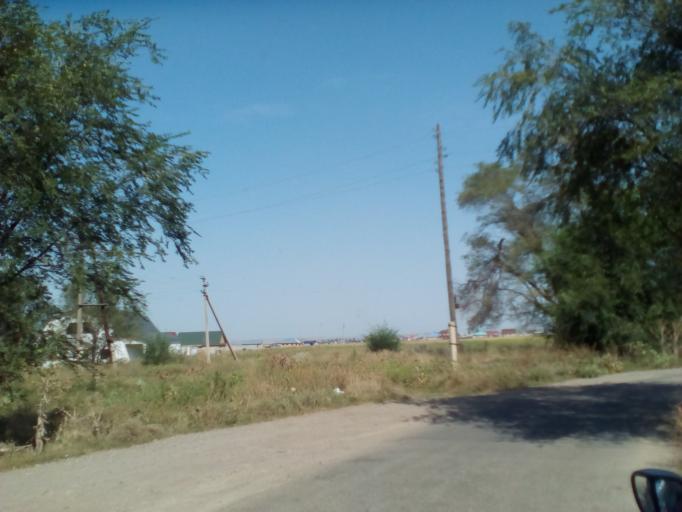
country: KZ
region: Almaty Oblysy
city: Burunday
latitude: 43.1638
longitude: 76.3862
